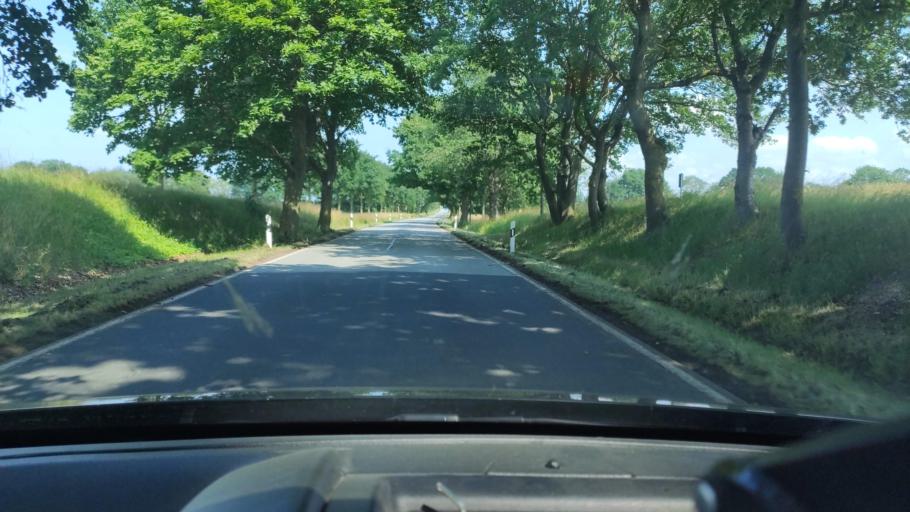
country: DE
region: Mecklenburg-Vorpommern
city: Grimmen
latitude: 54.0509
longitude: 13.0819
